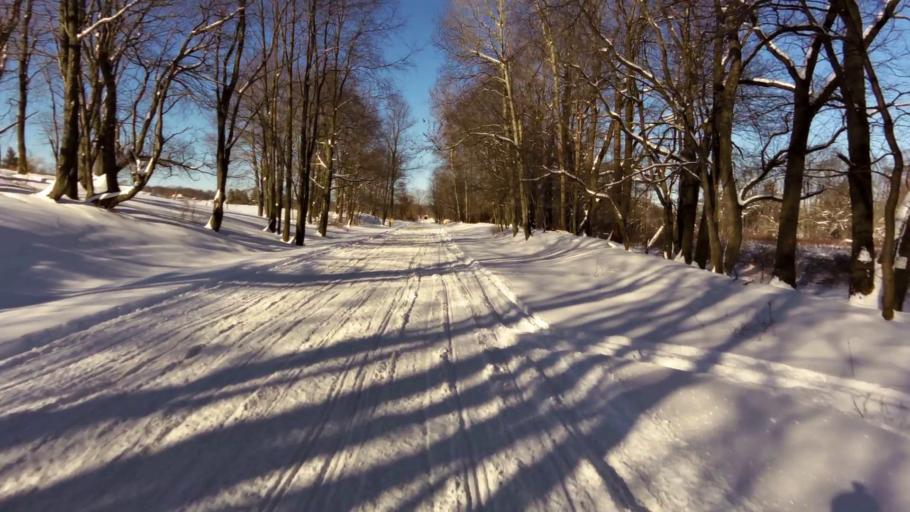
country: US
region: New York
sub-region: Chautauqua County
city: Mayville
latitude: 42.1716
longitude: -79.5829
